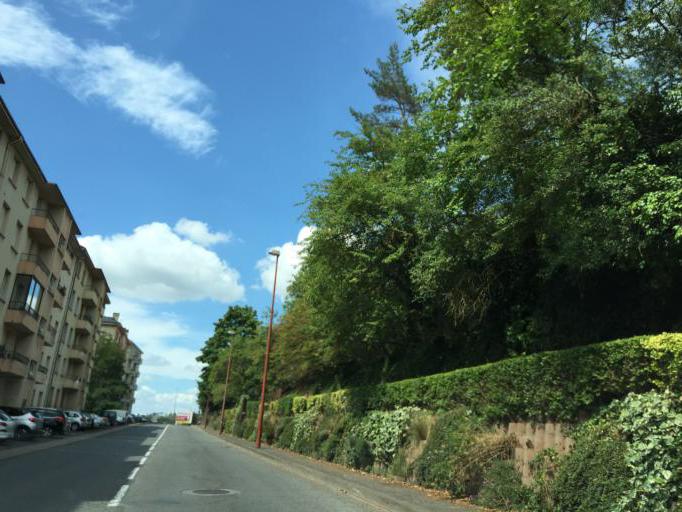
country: FR
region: Midi-Pyrenees
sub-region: Departement de l'Aveyron
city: Rodez
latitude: 44.3569
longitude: 2.5687
